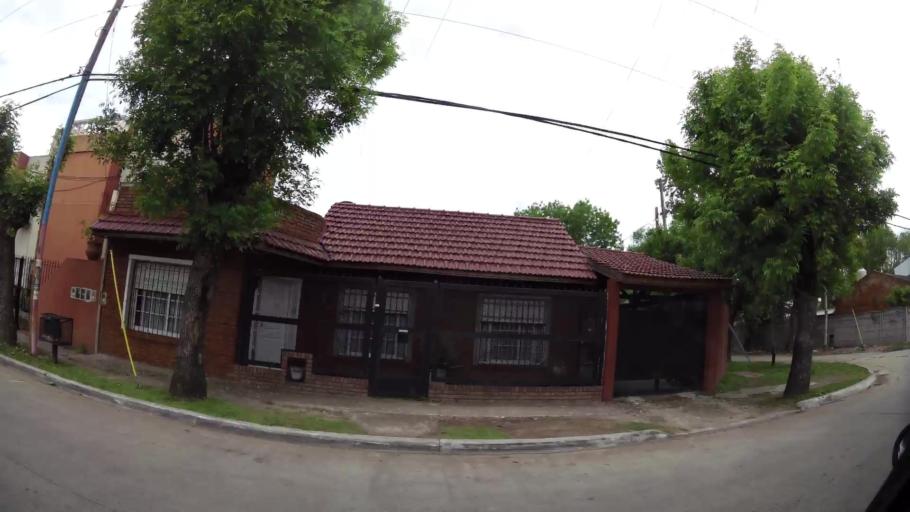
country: AR
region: Buenos Aires
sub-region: Partido de Quilmes
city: Quilmes
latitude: -34.7651
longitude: -58.2654
